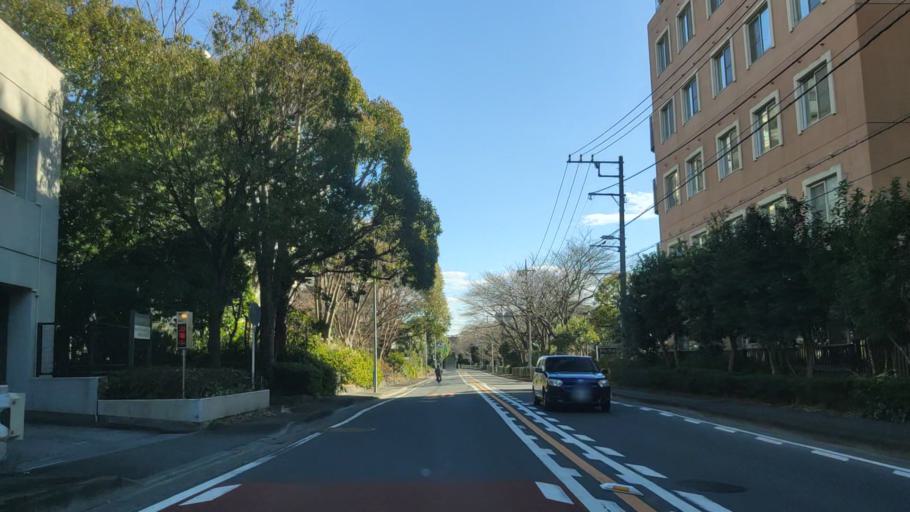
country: JP
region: Kanagawa
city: Minami-rinkan
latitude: 35.5040
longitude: 139.4937
